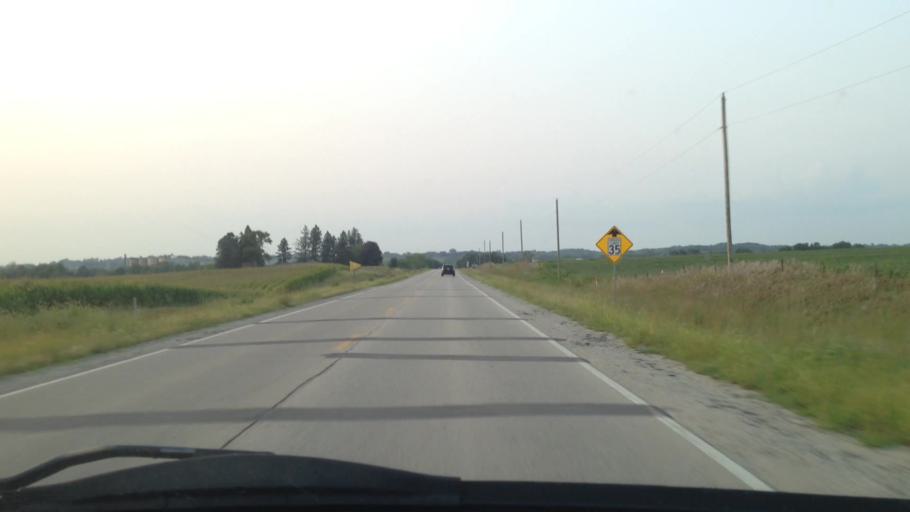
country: US
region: Iowa
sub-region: Linn County
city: Palo
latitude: 42.0821
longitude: -91.8689
